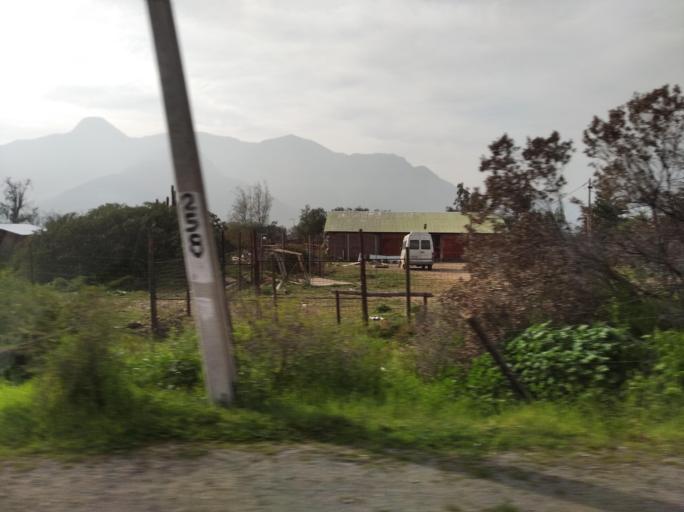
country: CL
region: Santiago Metropolitan
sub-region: Provincia de Chacabuco
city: Lampa
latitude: -33.2350
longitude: -70.9256
